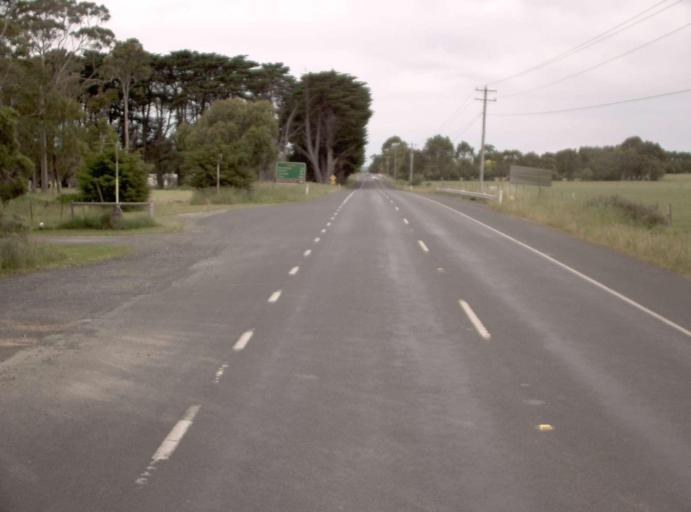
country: AU
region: Victoria
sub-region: Baw Baw
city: Warragul
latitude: -38.4923
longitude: 145.9520
